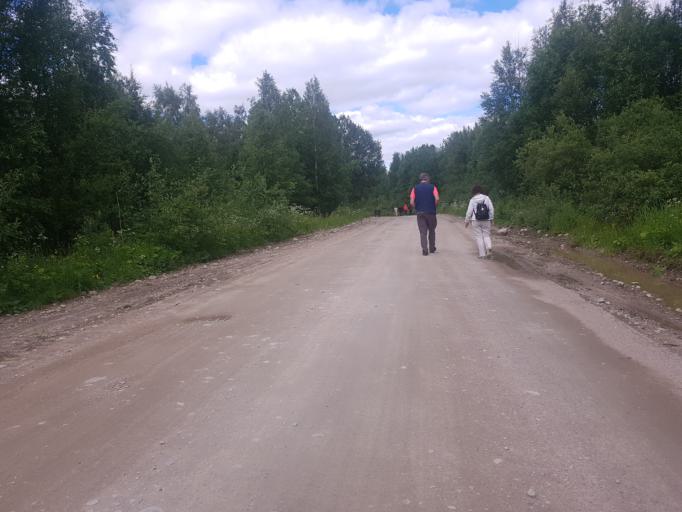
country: RU
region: Republic of Karelia
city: Kostomuksha
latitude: 65.1848
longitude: 30.2906
